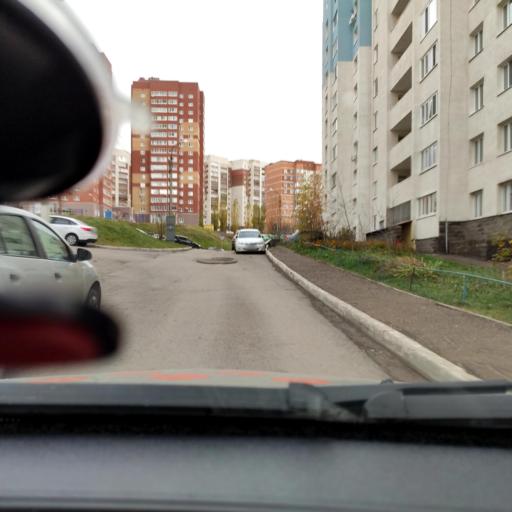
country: RU
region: Bashkortostan
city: Ufa
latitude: 54.6923
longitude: 55.9908
